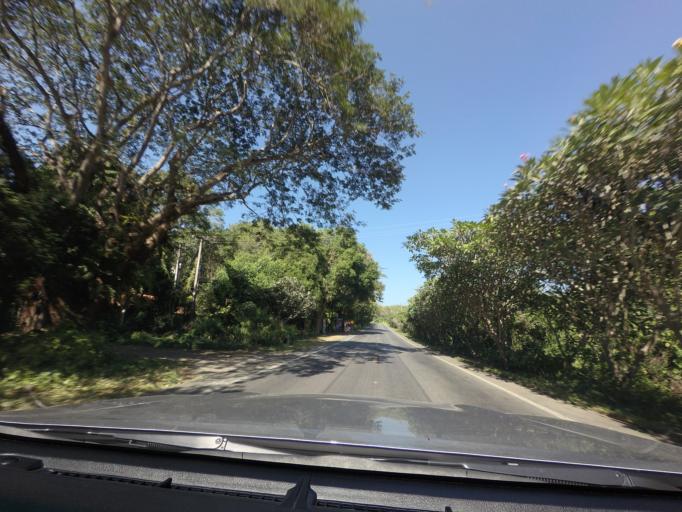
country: TH
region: Sukhothai
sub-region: Amphoe Si Satchanalai
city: Si Satchanalai
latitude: 17.6127
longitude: 99.7078
